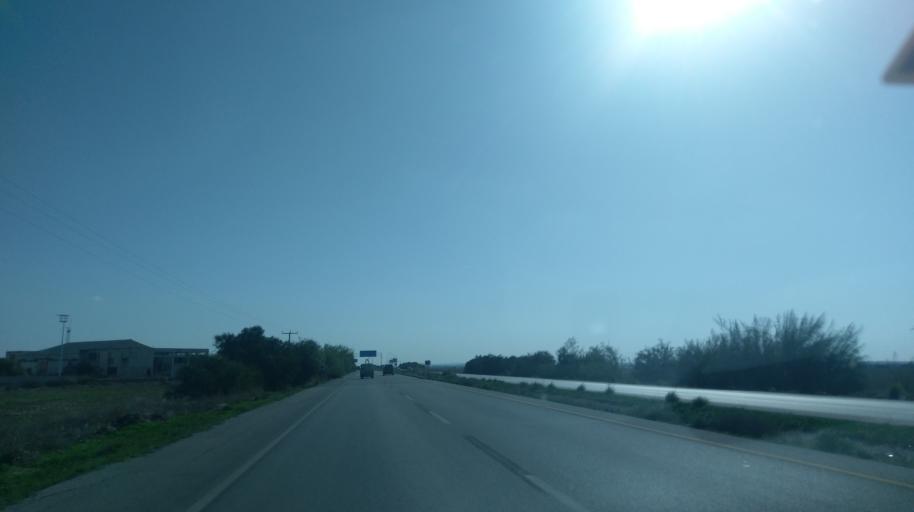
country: CY
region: Ammochostos
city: Acheritou
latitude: 35.1564
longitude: 33.8411
